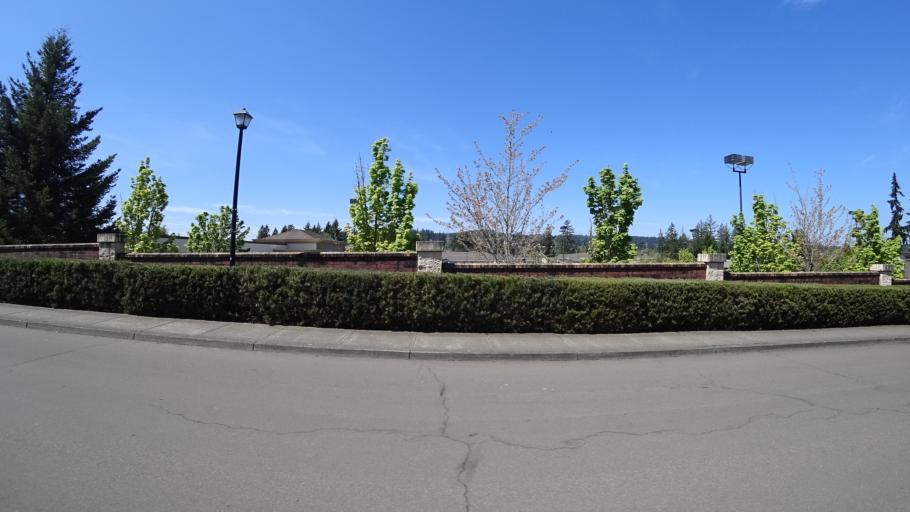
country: US
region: Oregon
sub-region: Washington County
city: King City
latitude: 45.4315
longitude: -122.8229
